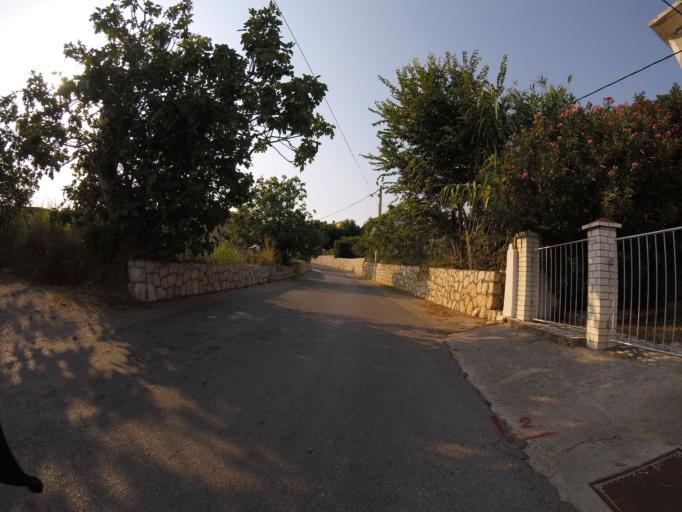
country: HR
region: Primorsko-Goranska
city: Lopar
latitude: 44.8324
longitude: 14.7298
